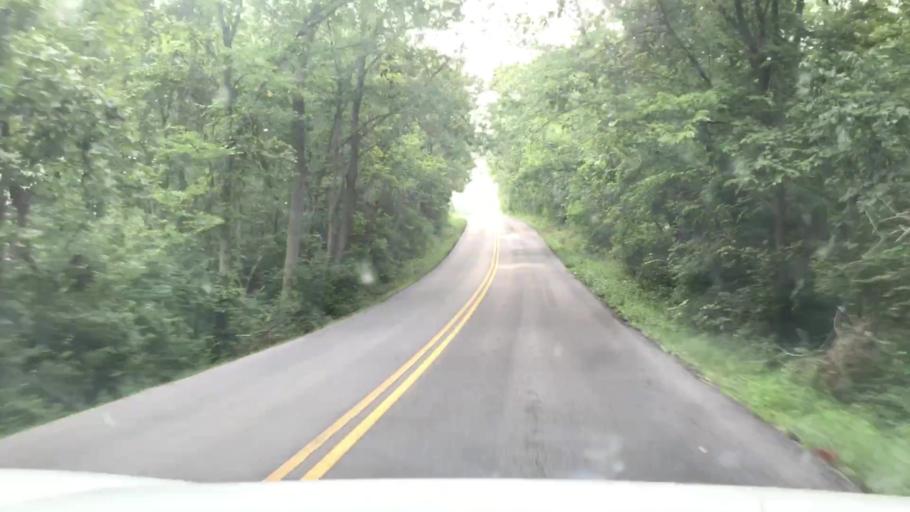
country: US
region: Missouri
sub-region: Saint Charles County
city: Cottleville
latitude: 38.7046
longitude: -90.6458
